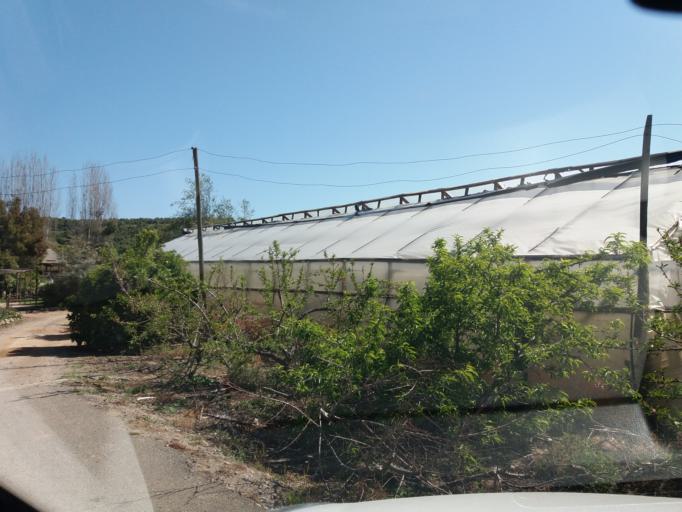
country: CL
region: Valparaiso
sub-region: Provincia de Marga Marga
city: Limache
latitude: -32.9491
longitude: -71.2855
